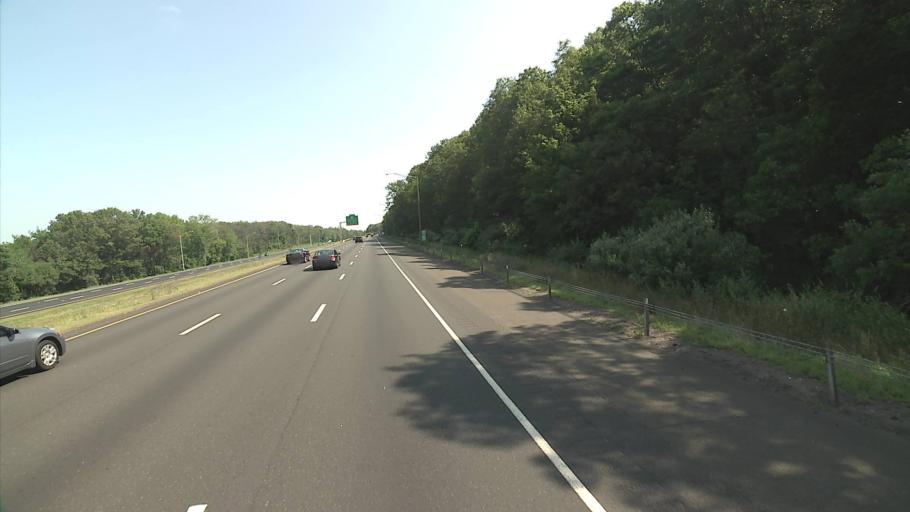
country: US
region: Connecticut
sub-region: New Haven County
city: North Haven
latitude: 41.4129
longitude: -72.8305
